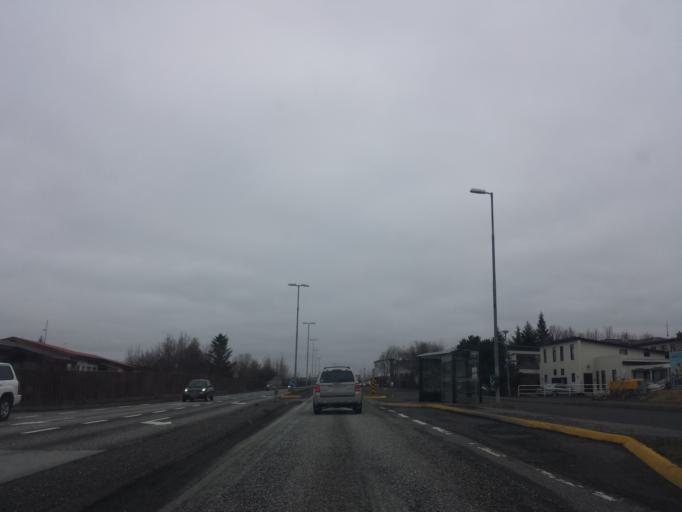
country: IS
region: Capital Region
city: Reykjavik
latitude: 64.1136
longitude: -21.8669
